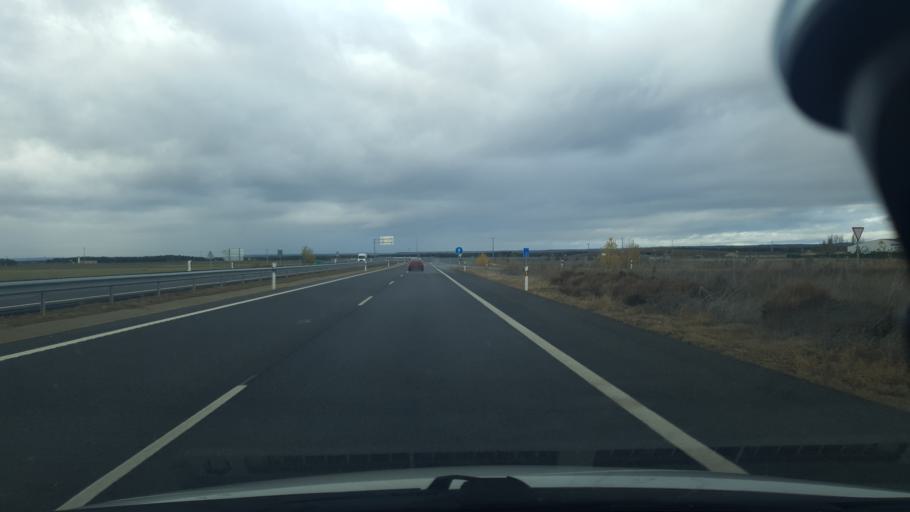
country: ES
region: Castille and Leon
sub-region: Provincia de Segovia
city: Sanchonuno
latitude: 41.3157
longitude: -4.3080
